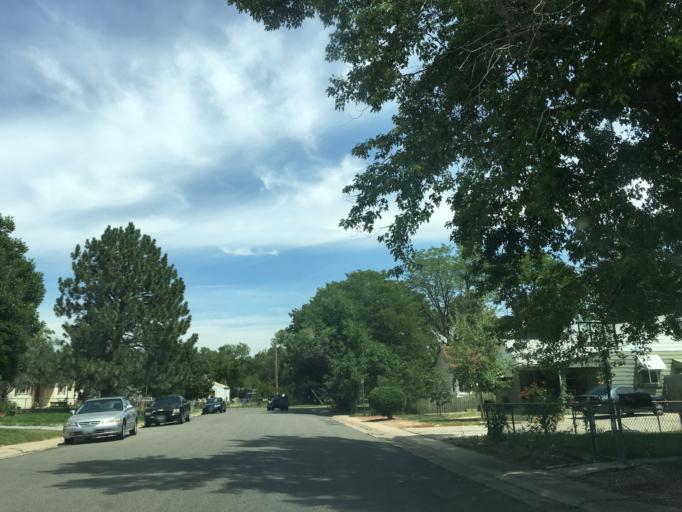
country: US
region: Colorado
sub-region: Jefferson County
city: Lakewood
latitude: 39.6942
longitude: -105.0379
